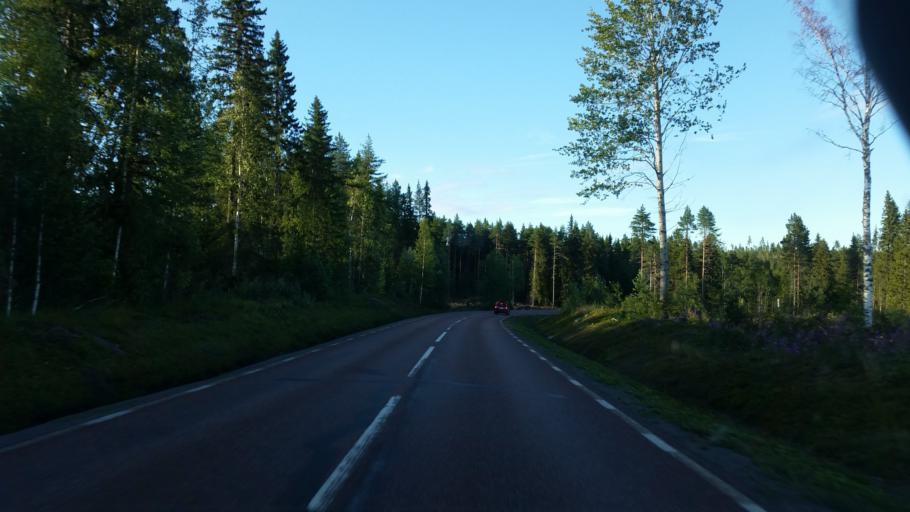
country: SE
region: Vaesterbotten
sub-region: Dorotea Kommun
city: Dorotea
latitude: 64.0675
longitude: 16.0478
